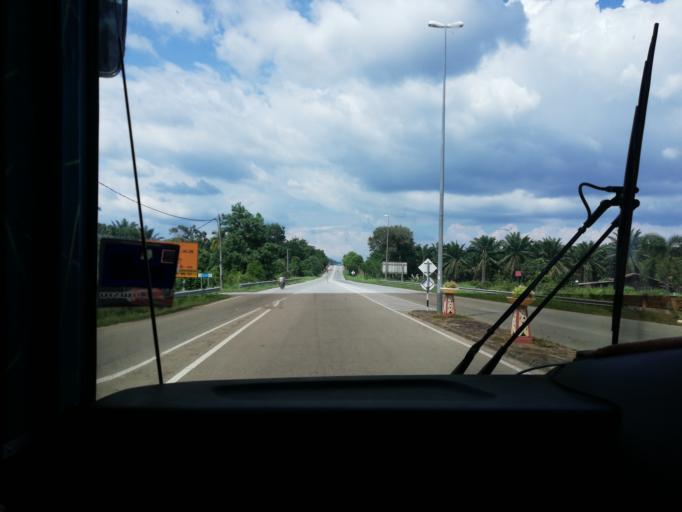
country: MY
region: Perak
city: Parit Buntar
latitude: 5.1091
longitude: 100.5524
